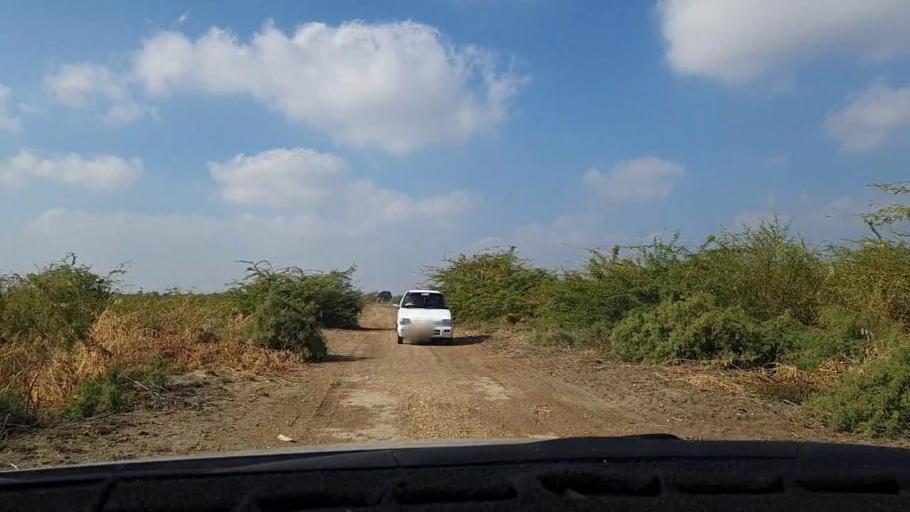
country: PK
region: Sindh
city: Tando Mittha Khan
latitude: 25.7710
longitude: 69.2621
